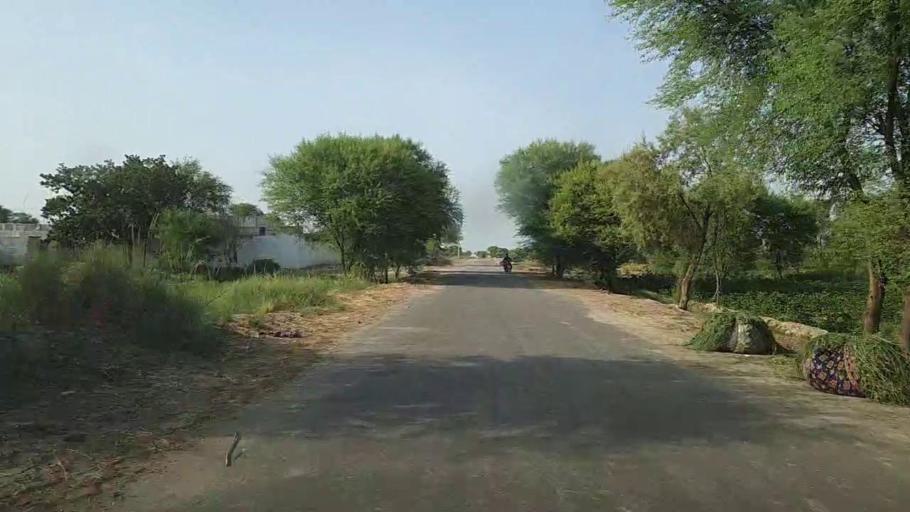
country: PK
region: Sindh
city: Ubauro
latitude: 28.0916
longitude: 69.8445
